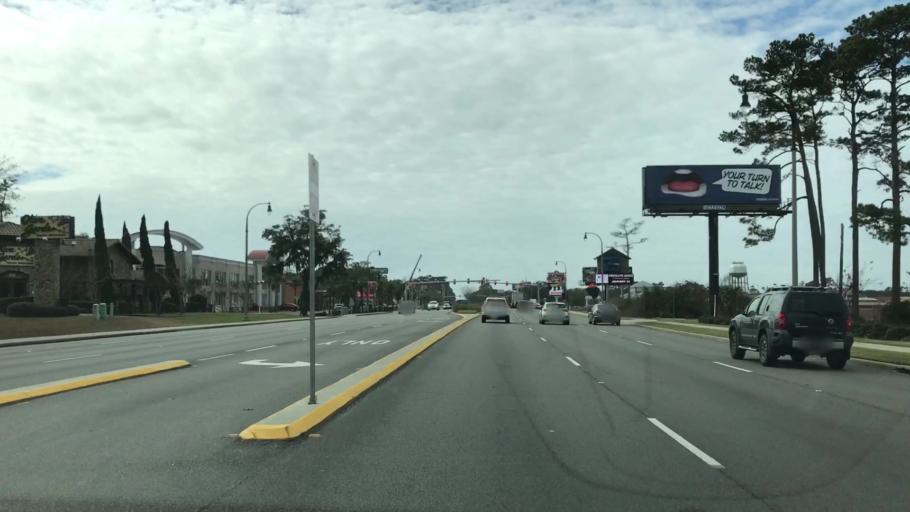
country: US
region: South Carolina
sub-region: Horry County
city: North Myrtle Beach
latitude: 33.7986
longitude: -78.7395
